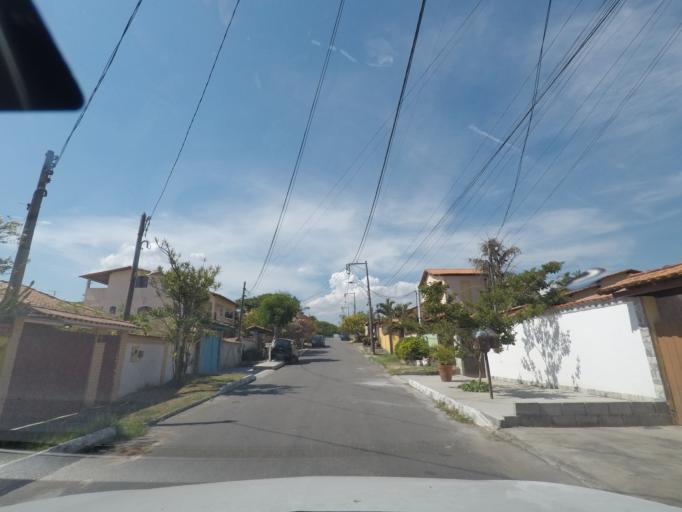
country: BR
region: Rio de Janeiro
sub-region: Marica
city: Marica
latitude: -22.9675
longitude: -42.9685
